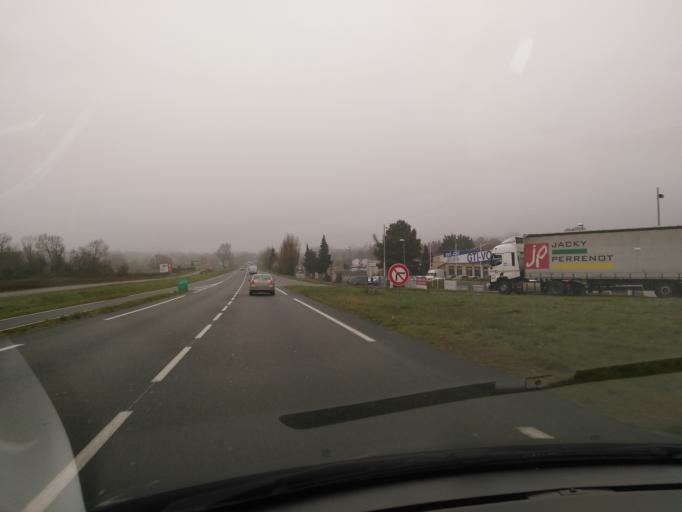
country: FR
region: Languedoc-Roussillon
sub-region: Departement de l'Aude
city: Carcassonne
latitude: 43.2158
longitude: 2.3231
